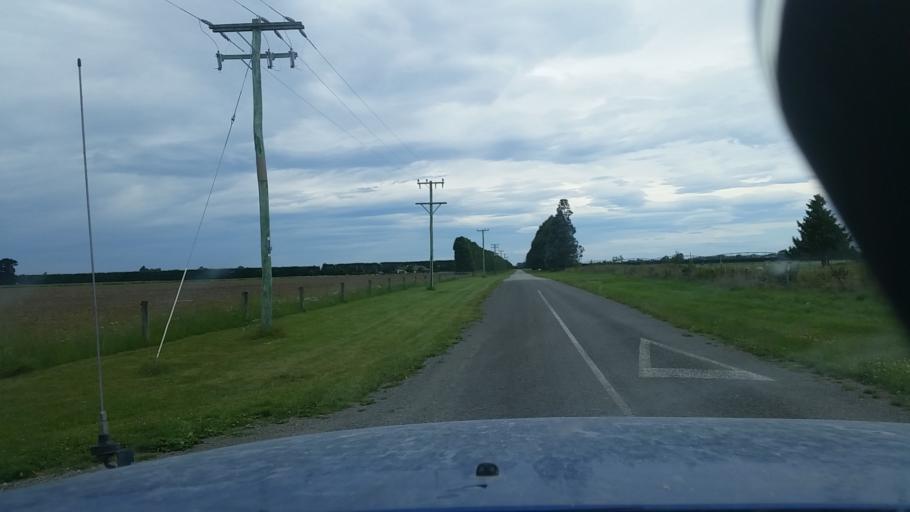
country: NZ
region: Canterbury
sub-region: Ashburton District
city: Tinwald
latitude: -43.9296
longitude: 171.6744
